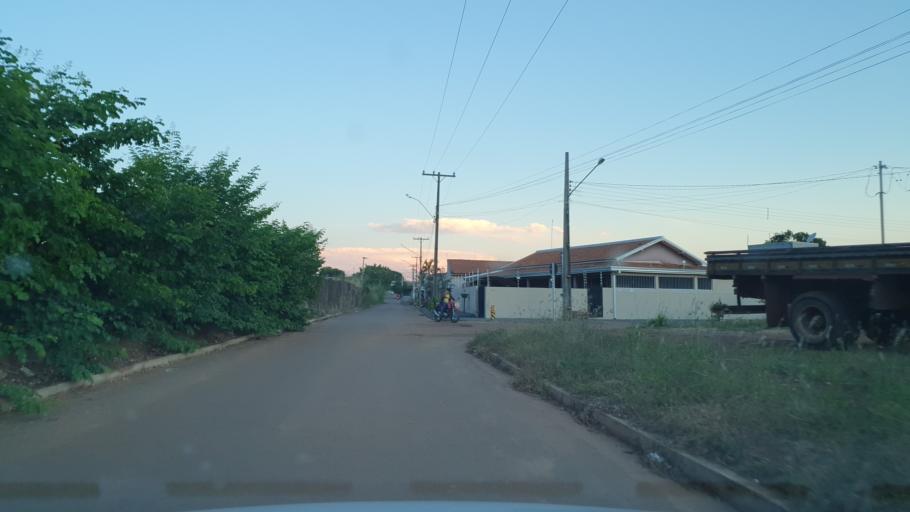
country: BR
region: Mato Grosso
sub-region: Pontes E Lacerda
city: Pontes e Lacerda
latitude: -15.2243
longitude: -59.3272
